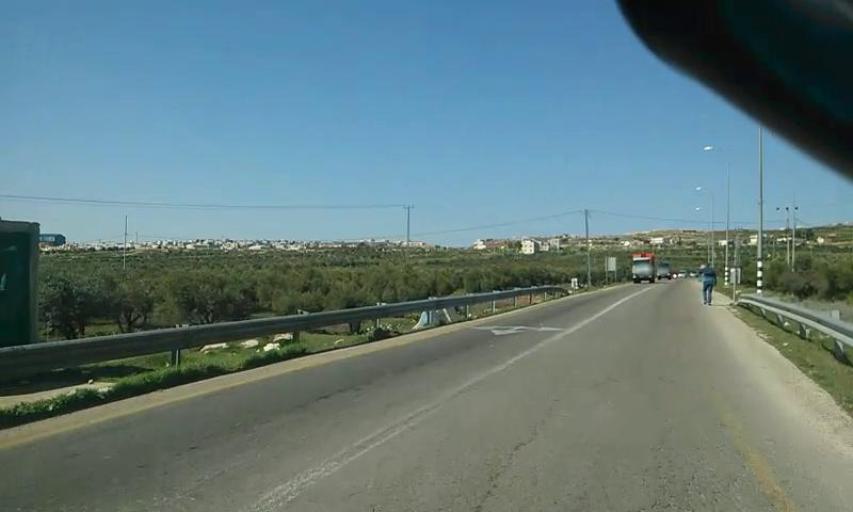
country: PS
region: West Bank
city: Marah Rabbah
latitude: 31.6408
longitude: 35.1995
